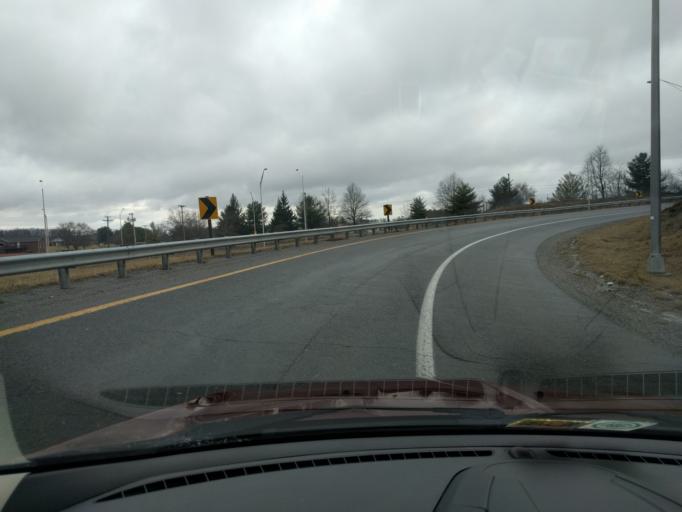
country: US
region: Virginia
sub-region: Montgomery County
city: Christiansburg
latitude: 37.1275
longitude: -80.3698
